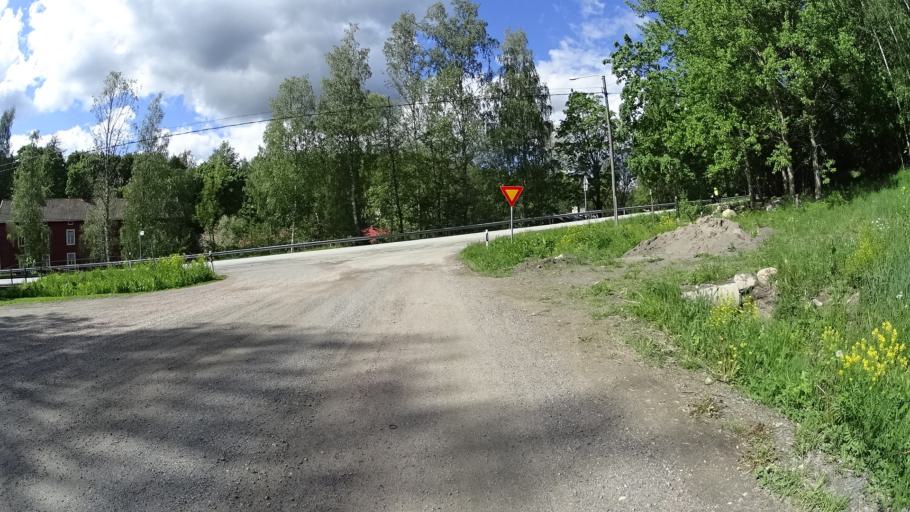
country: FI
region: Uusimaa
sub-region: Raaseporin
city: Pohja
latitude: 60.1722
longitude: 23.5936
